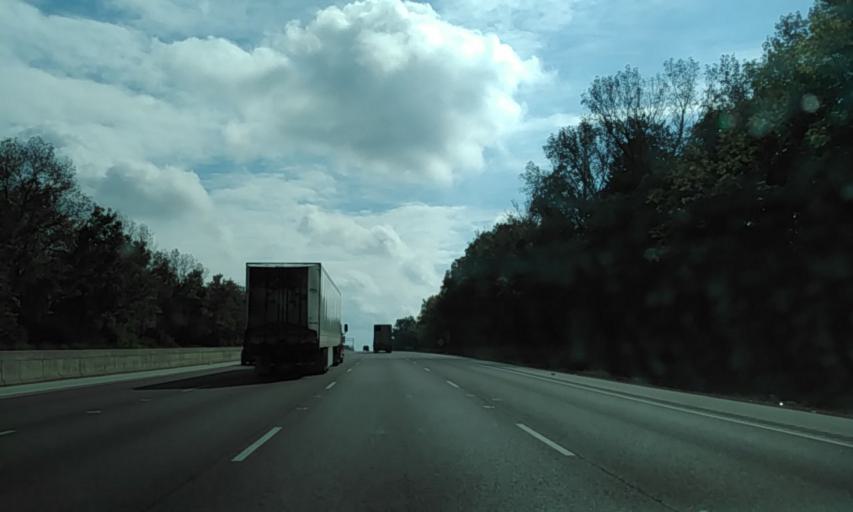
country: US
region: Illinois
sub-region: Saint Clair County
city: Caseyville
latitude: 38.6099
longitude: -90.0366
